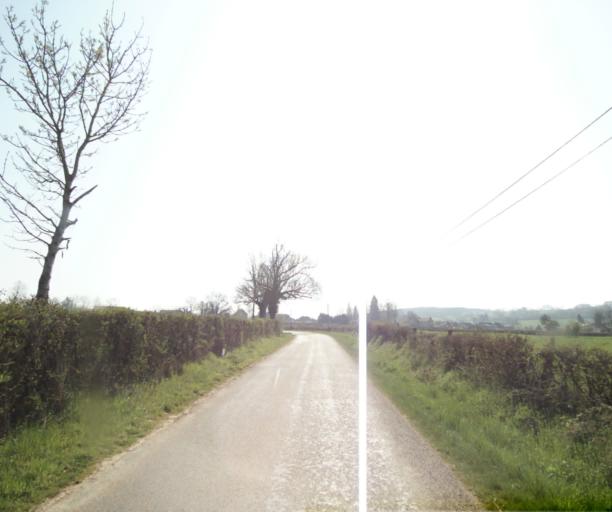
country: FR
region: Bourgogne
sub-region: Departement de Saone-et-Loire
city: Charolles
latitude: 46.4754
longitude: 4.3311
